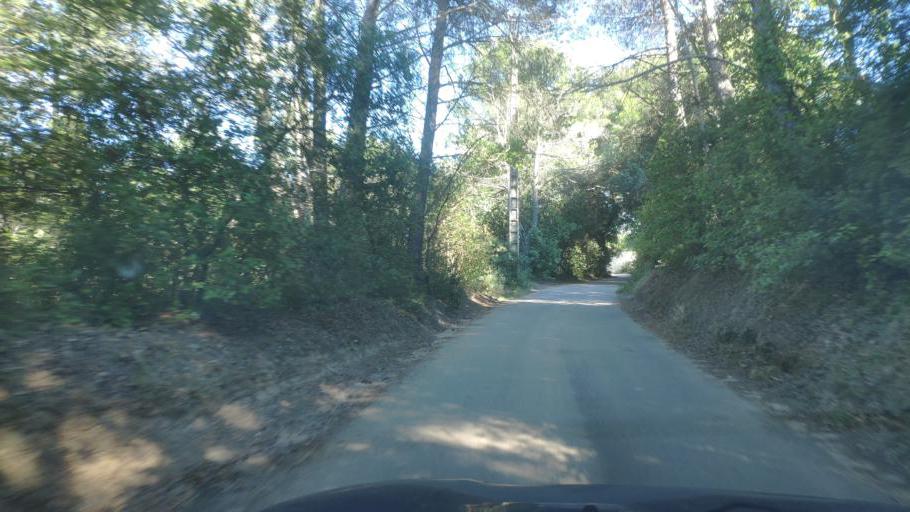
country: FR
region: Provence-Alpes-Cote d'Azur
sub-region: Departement du Vaucluse
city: Aubignan
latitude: 44.0840
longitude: 5.0420
